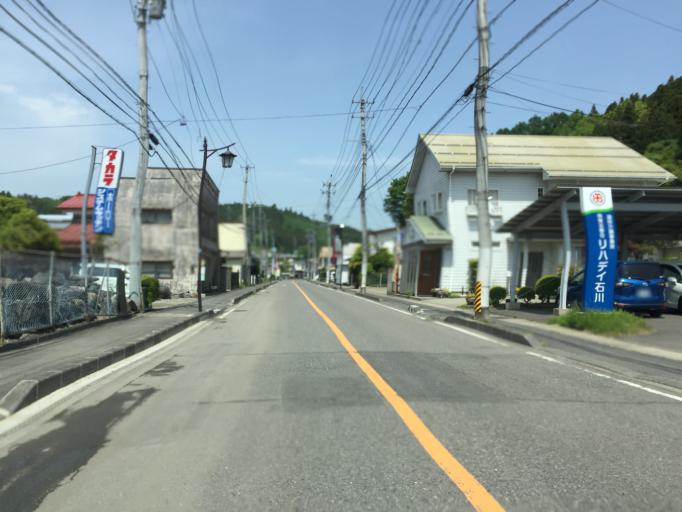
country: JP
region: Fukushima
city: Ishikawa
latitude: 37.1522
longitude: 140.4568
